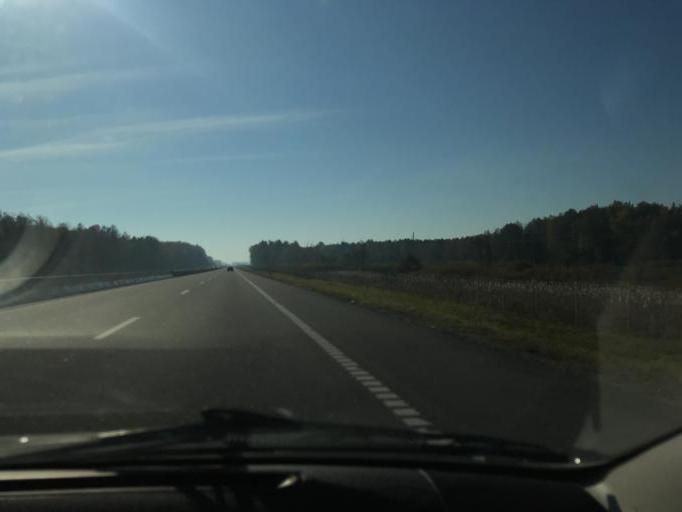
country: BY
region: Minsk
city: Slutsk
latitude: 53.2507
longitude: 27.5501
